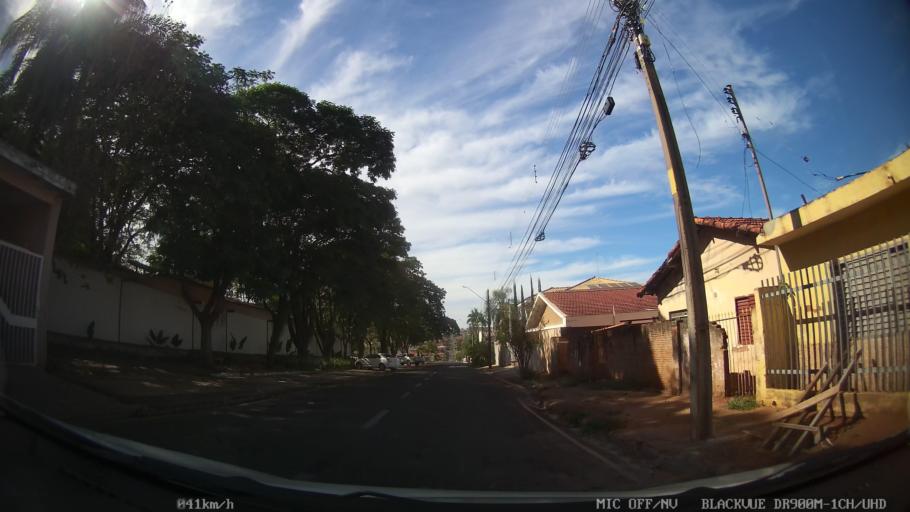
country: BR
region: Sao Paulo
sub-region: Catanduva
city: Catanduva
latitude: -21.1274
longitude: -48.9647
